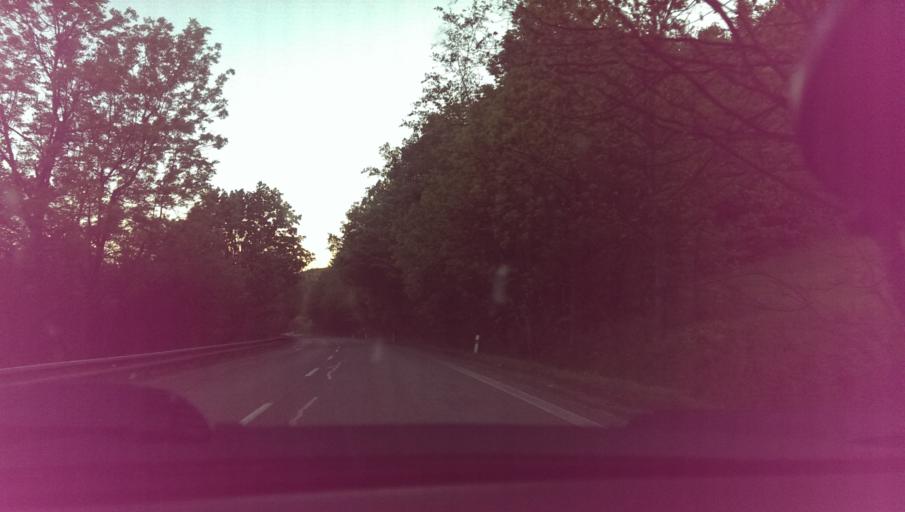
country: CZ
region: Zlin
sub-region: Okres Vsetin
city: Dolni Becva
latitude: 49.4918
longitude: 18.1718
